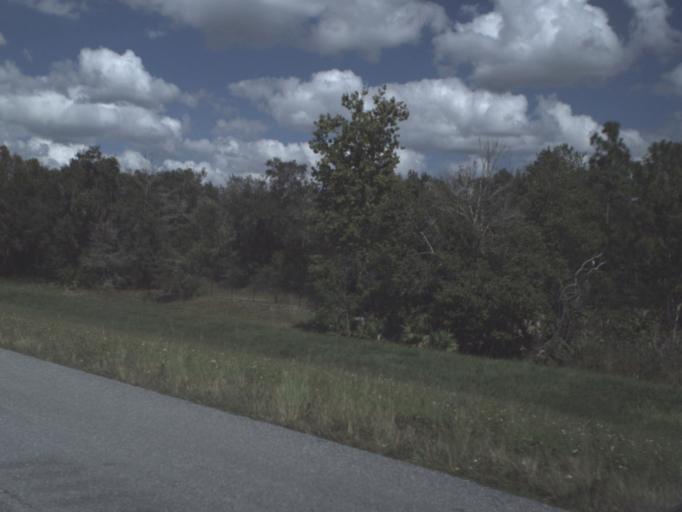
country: US
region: Florida
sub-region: Pasco County
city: Shady Hills
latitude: 28.3149
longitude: -82.5506
